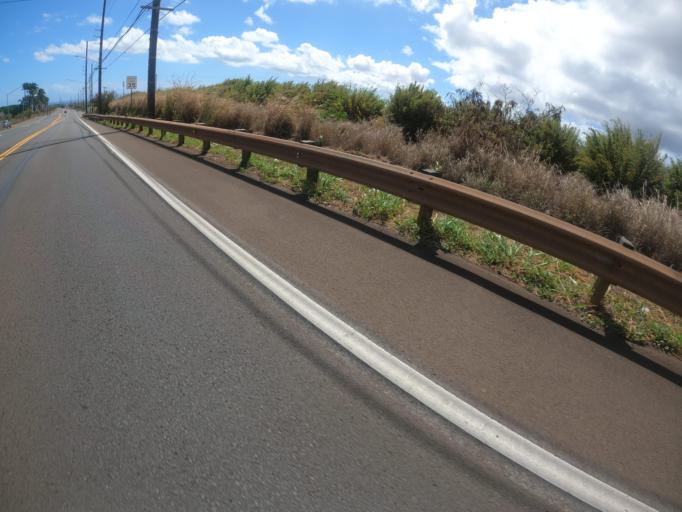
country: US
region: Hawaii
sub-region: Honolulu County
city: Village Park
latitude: 21.3988
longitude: -158.0391
